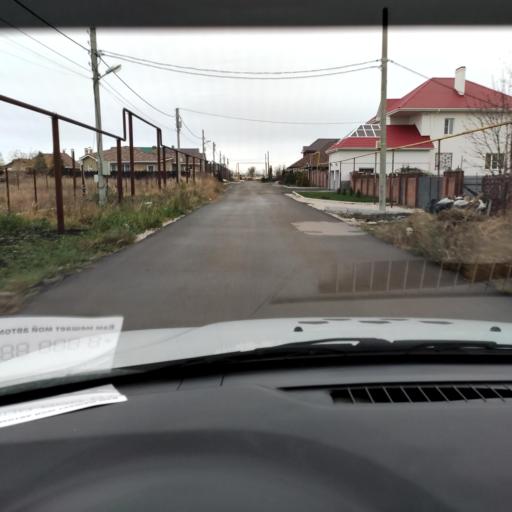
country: RU
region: Samara
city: Podstepki
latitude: 53.5133
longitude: 49.2081
